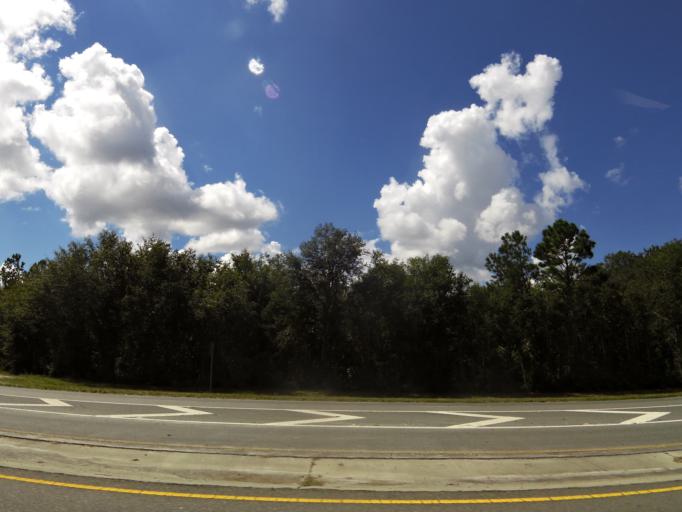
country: US
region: Georgia
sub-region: Charlton County
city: Folkston
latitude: 30.8227
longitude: -82.0030
